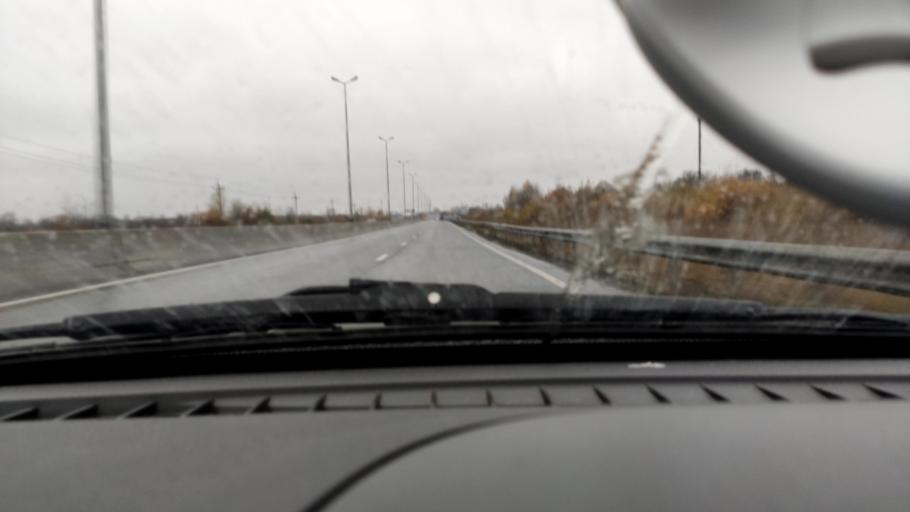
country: RU
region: Perm
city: Kondratovo
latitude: 58.0056
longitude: 56.0670
